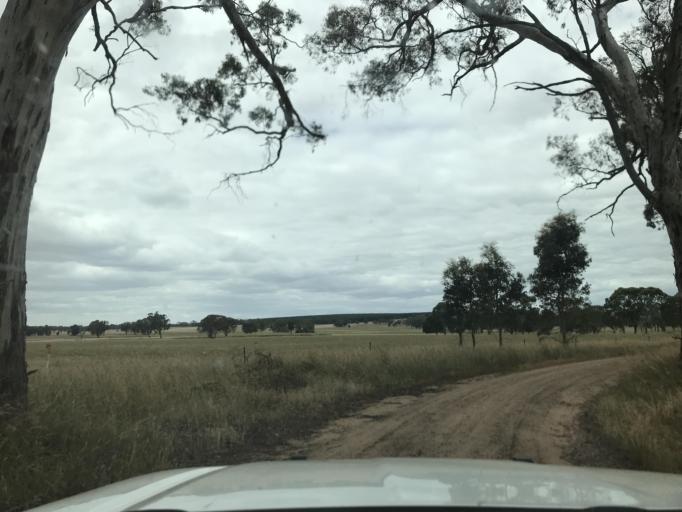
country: AU
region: South Australia
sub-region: Naracoorte and Lucindale
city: Naracoorte
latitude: -36.9244
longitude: 141.3019
